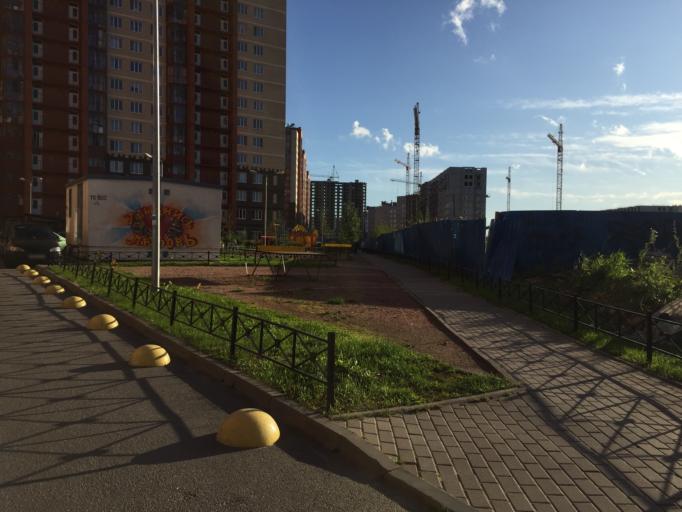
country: RU
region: Leningrad
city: Murino
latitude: 60.0651
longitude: 30.4572
